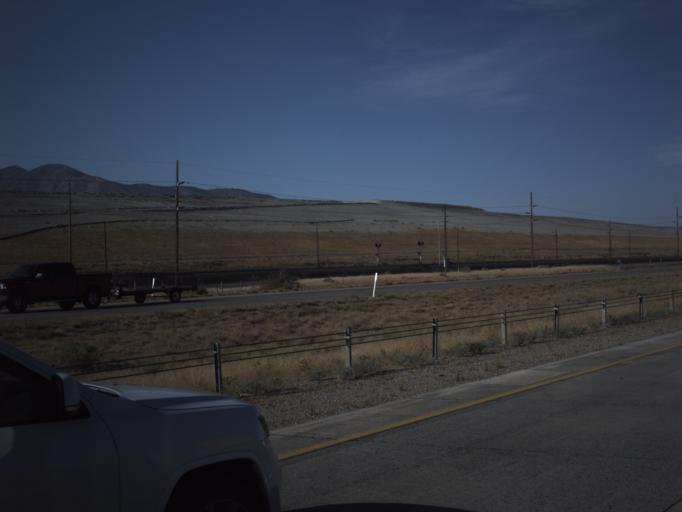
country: US
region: Utah
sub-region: Salt Lake County
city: Magna
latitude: 40.7710
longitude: -112.1227
